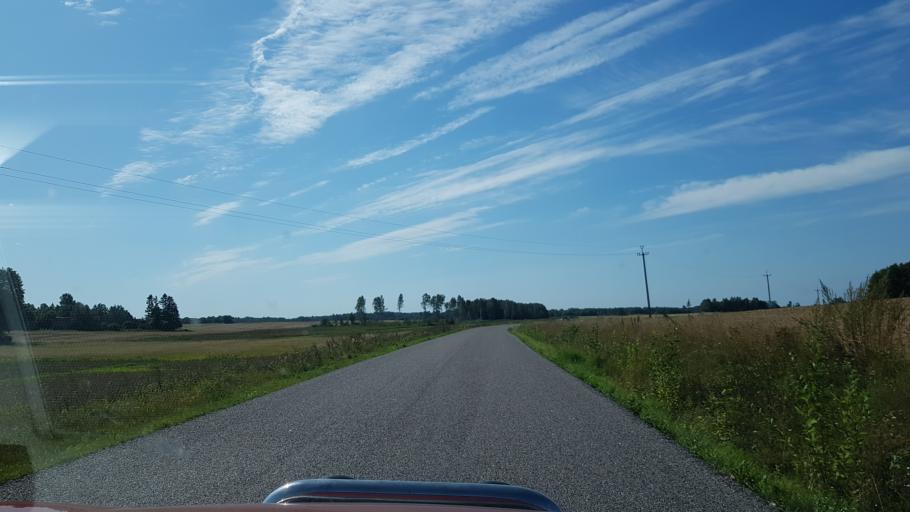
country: EE
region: Tartu
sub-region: Puhja vald
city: Puhja
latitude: 58.2613
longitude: 26.2964
